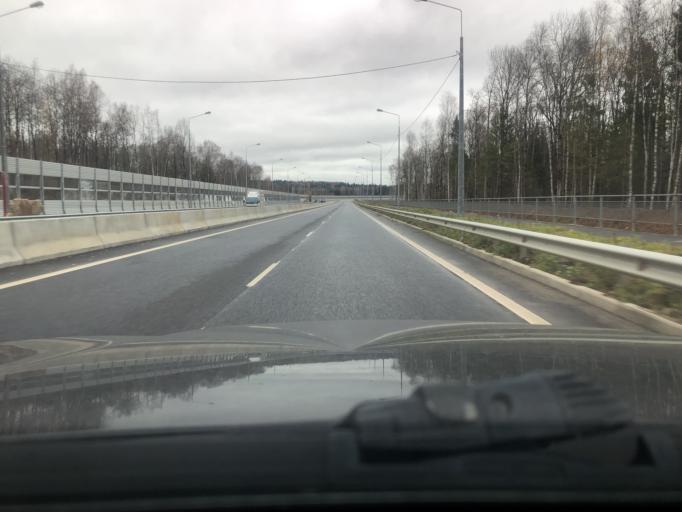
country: RU
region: Moskovskaya
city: Semkhoz
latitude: 56.3352
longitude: 38.0890
